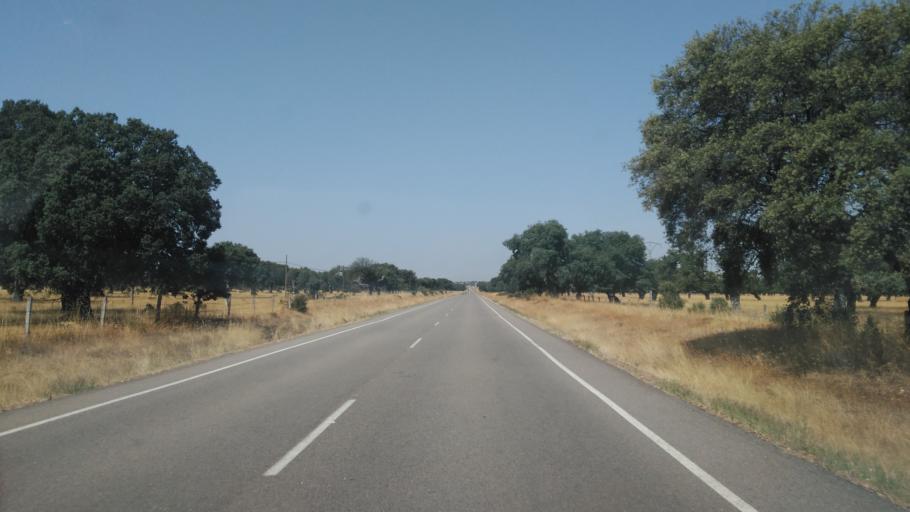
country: ES
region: Castille and Leon
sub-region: Provincia de Salamanca
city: Cabrillas
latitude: 40.7270
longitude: -6.1580
